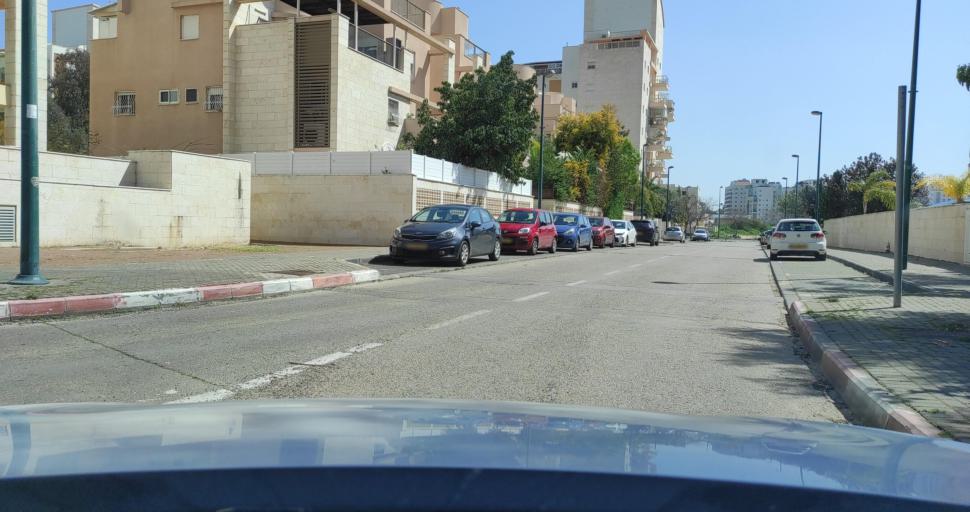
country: IL
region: Central District
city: Nordiyya
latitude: 32.3077
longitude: 34.8714
